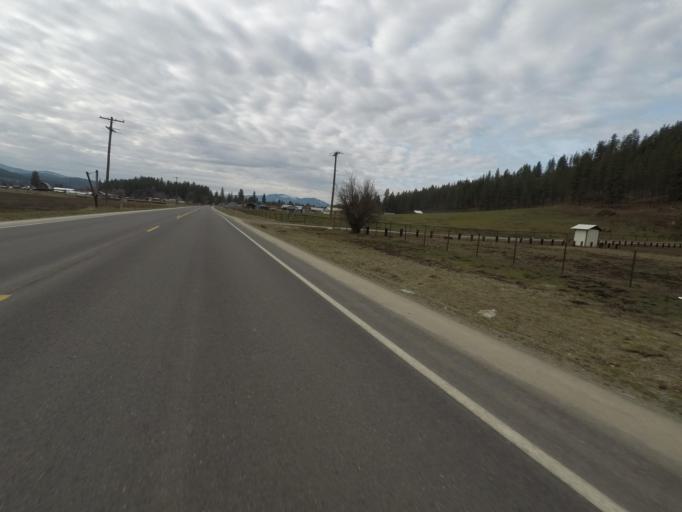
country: US
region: Washington
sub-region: Stevens County
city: Colville
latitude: 48.5635
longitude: -117.8796
